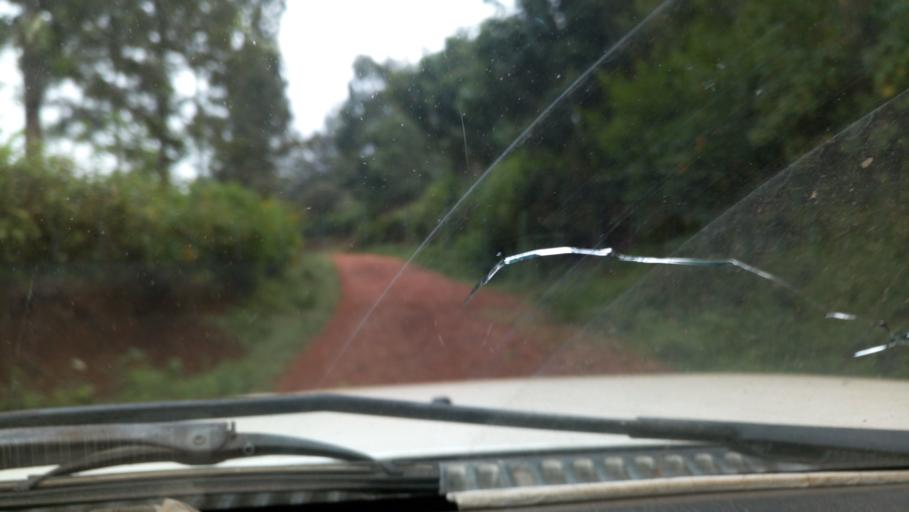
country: KE
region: Murang'a District
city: Kangema
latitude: -0.6860
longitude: 37.0237
